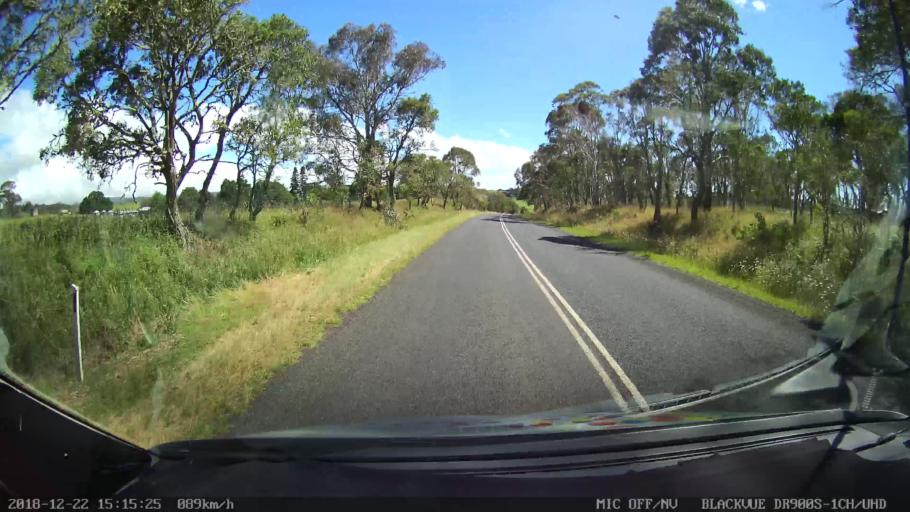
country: AU
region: New South Wales
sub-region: Bellingen
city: Dorrigo
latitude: -30.3788
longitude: 152.3672
